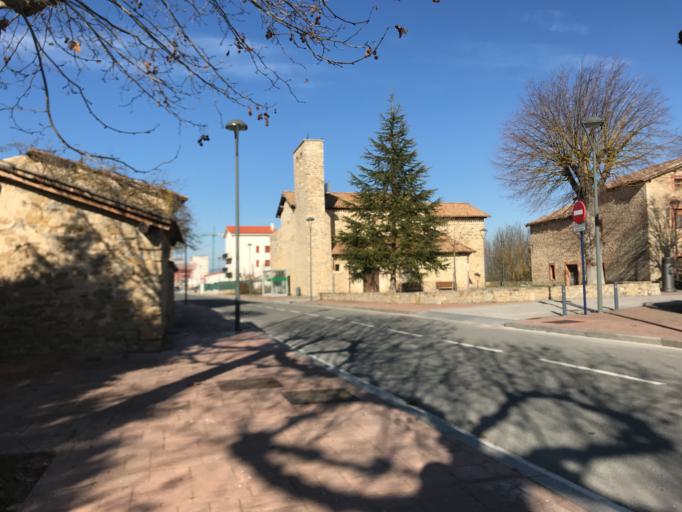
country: ES
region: Basque Country
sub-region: Provincia de Alava
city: Gasteiz / Vitoria
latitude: 42.8236
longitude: -2.6764
